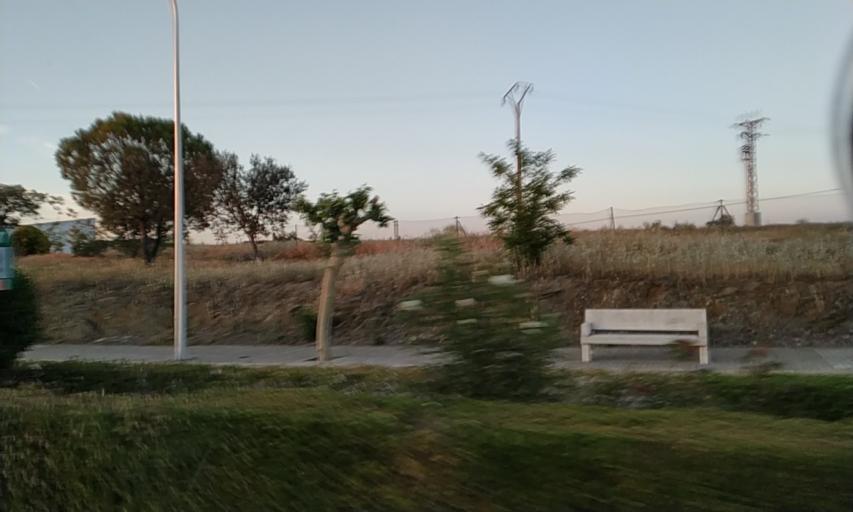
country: ES
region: Extremadura
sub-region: Provincia de Caceres
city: Alcantara
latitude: 39.7098
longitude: -6.8860
